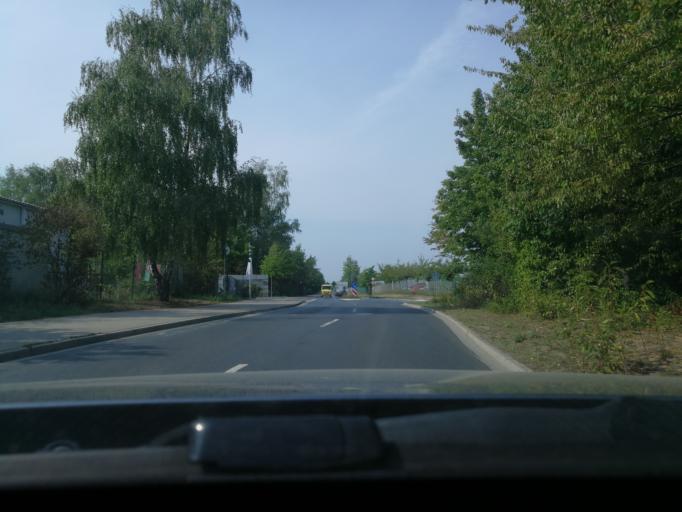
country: DE
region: North Rhine-Westphalia
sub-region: Regierungsbezirk Dusseldorf
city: Dusseldorf
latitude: 51.1596
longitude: 6.7574
